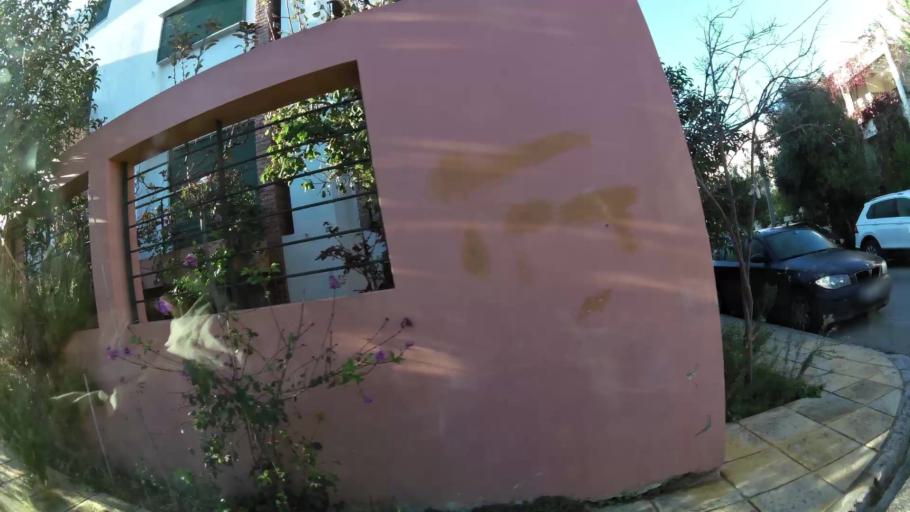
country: GR
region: Attica
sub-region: Nomarchia Athinas
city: Vrilissia
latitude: 38.0326
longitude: 23.8424
